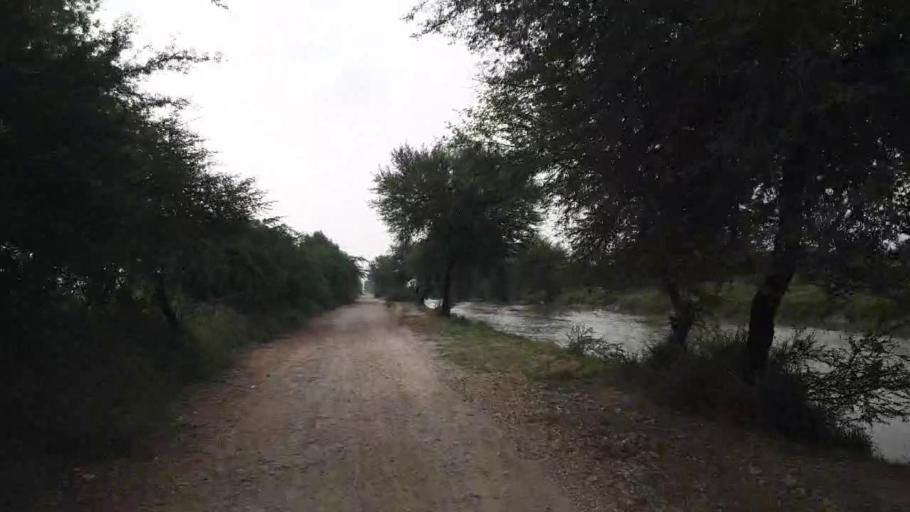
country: PK
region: Sindh
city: Kario
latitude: 24.8700
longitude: 68.5176
